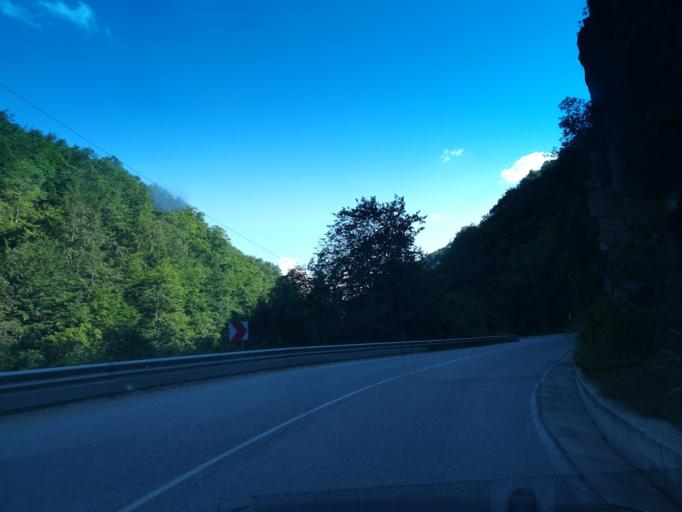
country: BG
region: Smolyan
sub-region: Obshtina Chepelare
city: Chepelare
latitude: 41.7851
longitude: 24.7084
